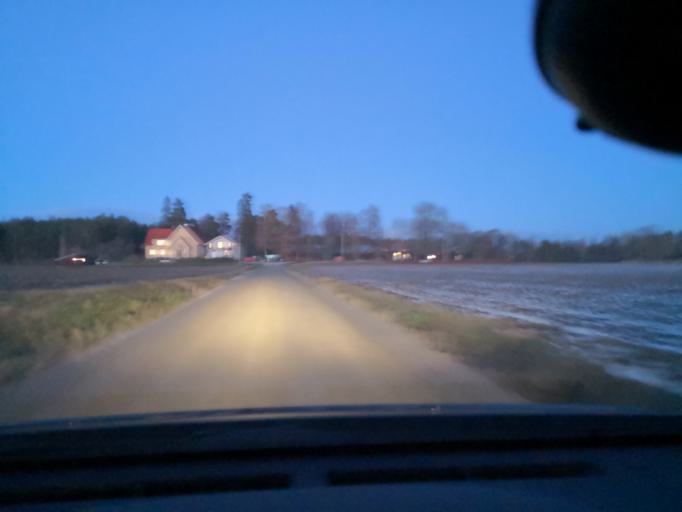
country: SE
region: Vaestmanland
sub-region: Sala Kommun
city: Sala
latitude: 59.8752
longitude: 16.6955
